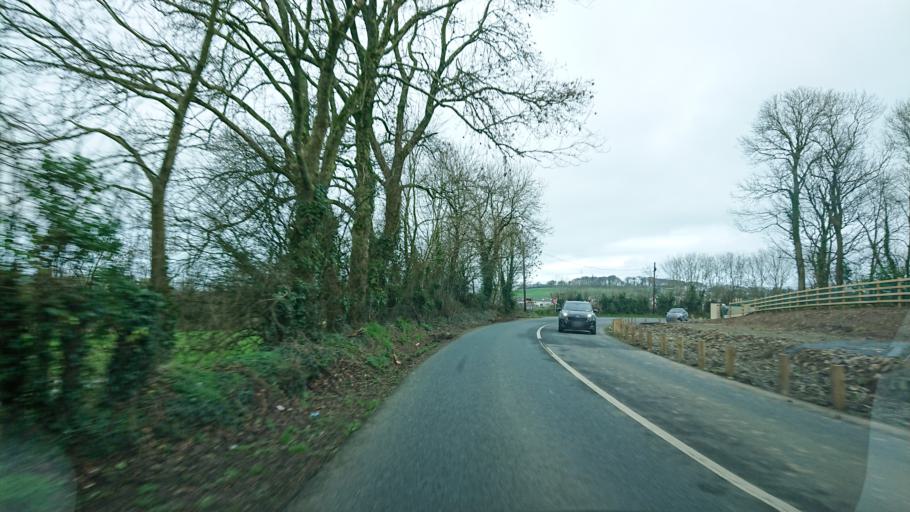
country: IE
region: Leinster
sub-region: Kilkenny
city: Mooncoin
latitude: 52.2245
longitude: -7.2388
